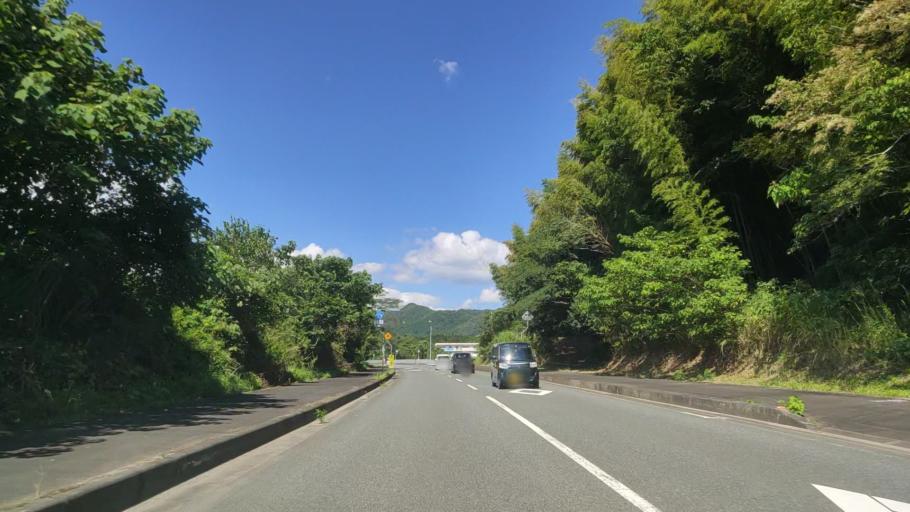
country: JP
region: Kyoto
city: Fukuchiyama
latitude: 35.2322
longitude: 135.1280
